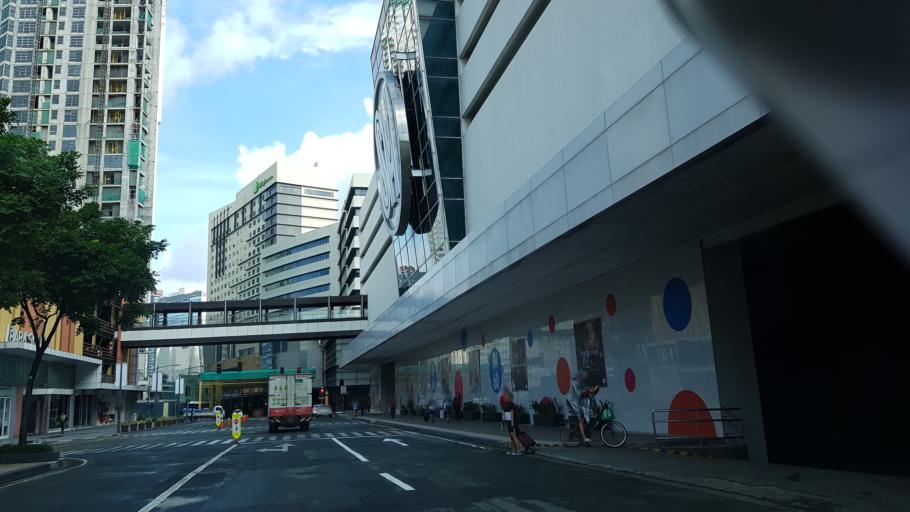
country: PH
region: Metro Manila
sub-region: Makati City
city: Makati City
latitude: 14.5490
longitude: 121.0265
